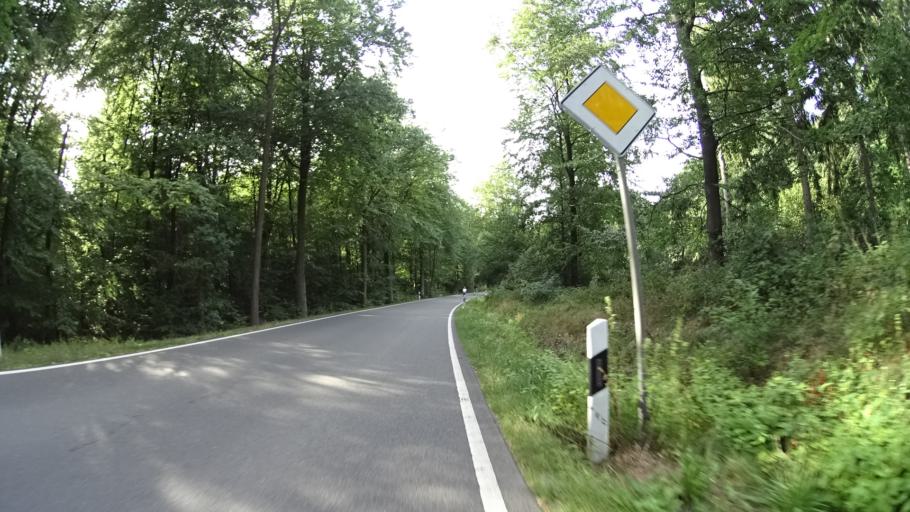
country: DE
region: Lower Saxony
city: Undeloh
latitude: 53.1640
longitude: 9.8962
